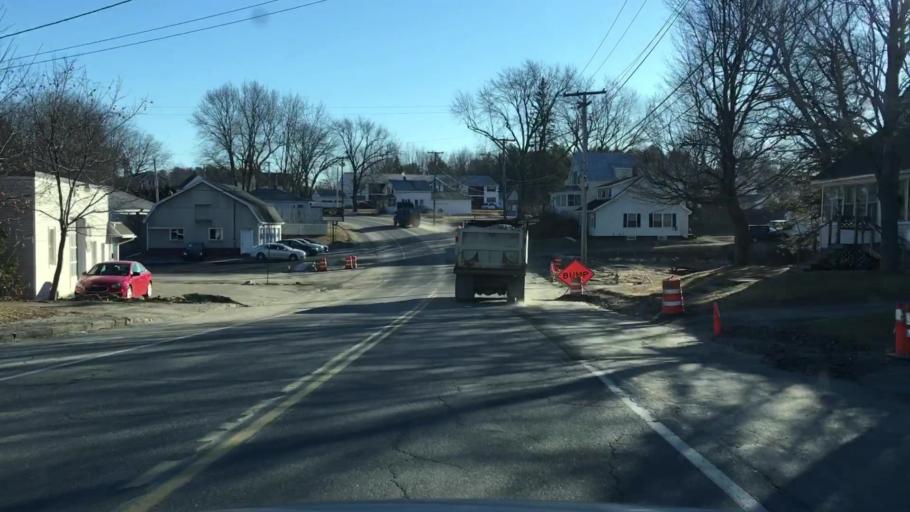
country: US
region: Maine
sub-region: Kennebec County
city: Winslow
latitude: 44.5423
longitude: -69.6210
